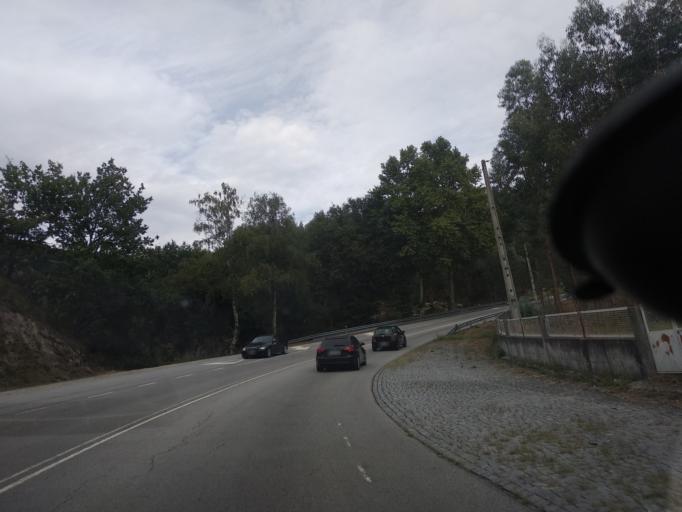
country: PT
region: Braga
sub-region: Povoa de Lanhoso
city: Povoa de Lanhoso
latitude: 41.6151
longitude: -8.2409
